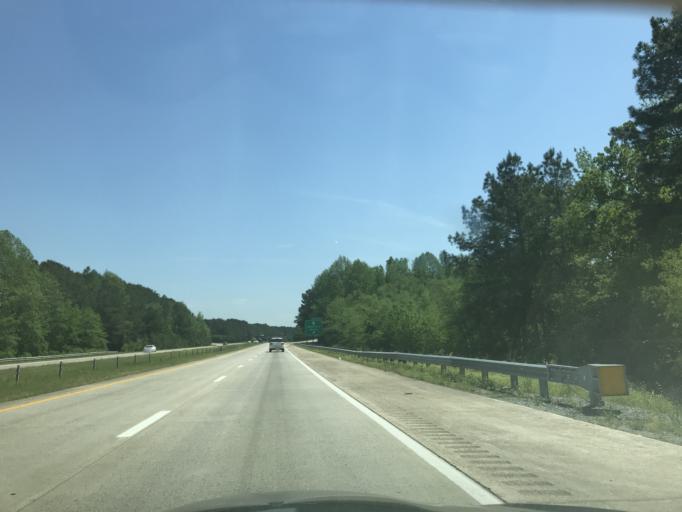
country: US
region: North Carolina
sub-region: Johnston County
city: Benson
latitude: 35.5212
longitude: -78.5611
